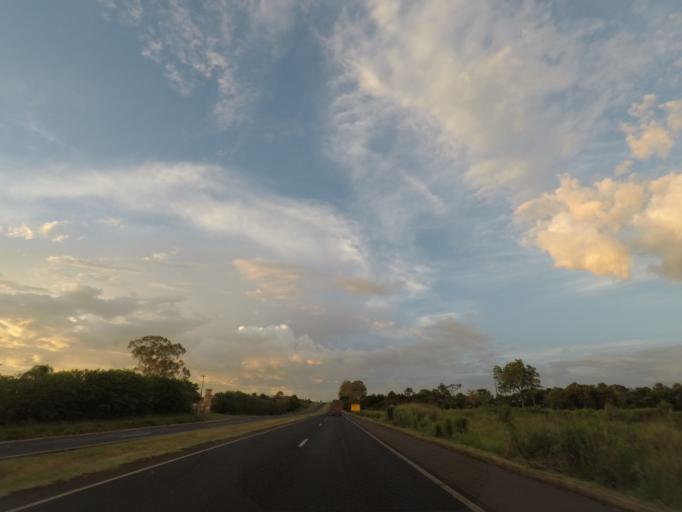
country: BR
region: Minas Gerais
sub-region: Uberaba
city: Uberaba
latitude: -19.6774
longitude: -47.9956
